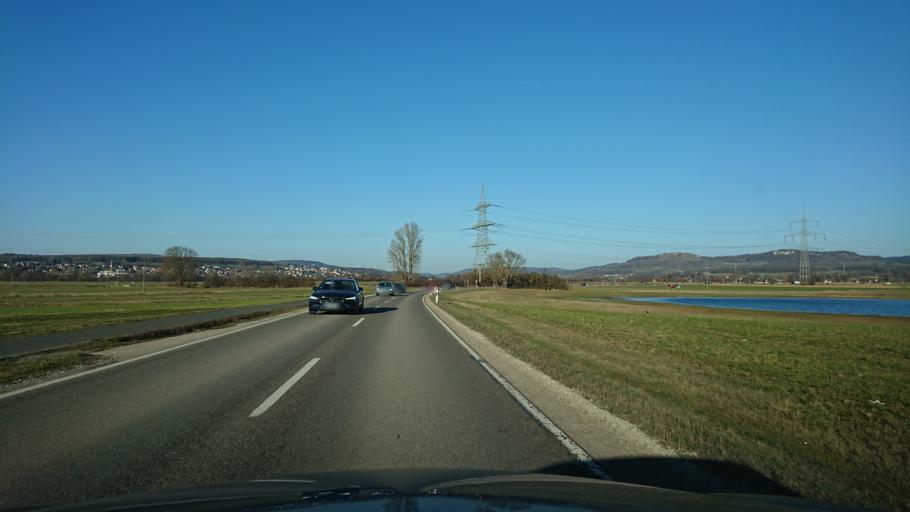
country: DE
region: Bavaria
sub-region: Upper Franconia
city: Pinzberg
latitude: 49.6959
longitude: 11.0881
